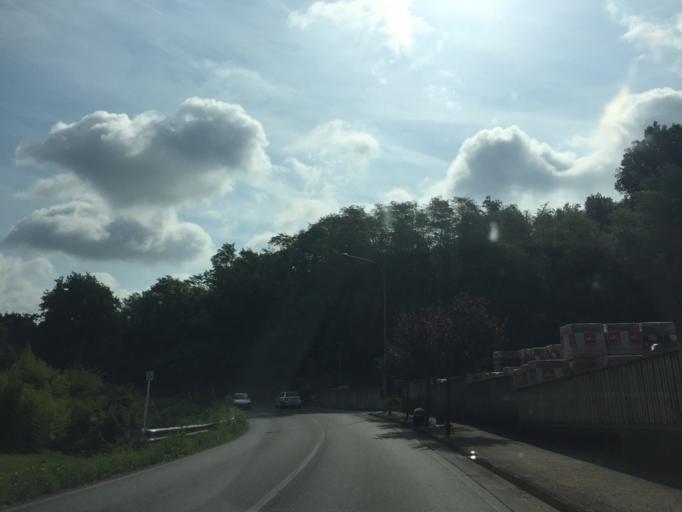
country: IT
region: Tuscany
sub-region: Provincia di Pistoia
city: Lamporecchio
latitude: 43.8174
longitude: 10.8895
